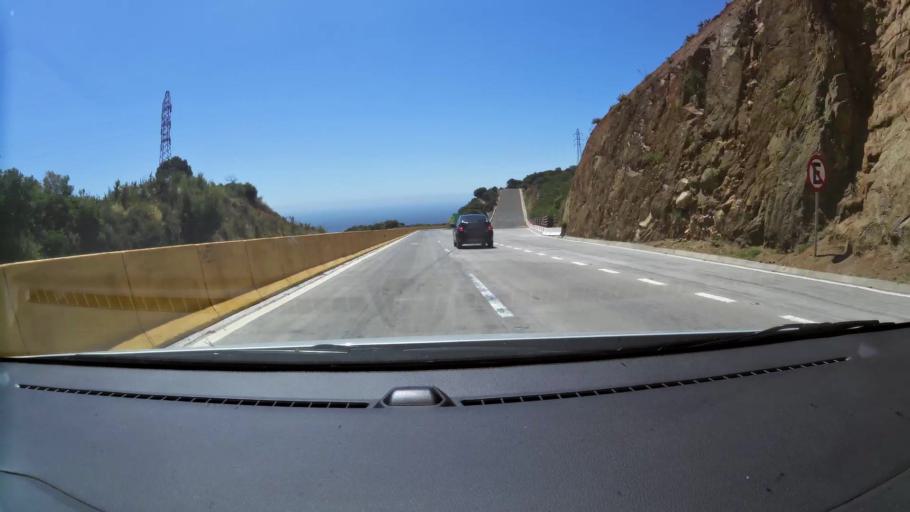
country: CL
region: Valparaiso
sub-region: Provincia de Valparaiso
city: Valparaiso
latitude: -33.0535
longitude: -71.6549
